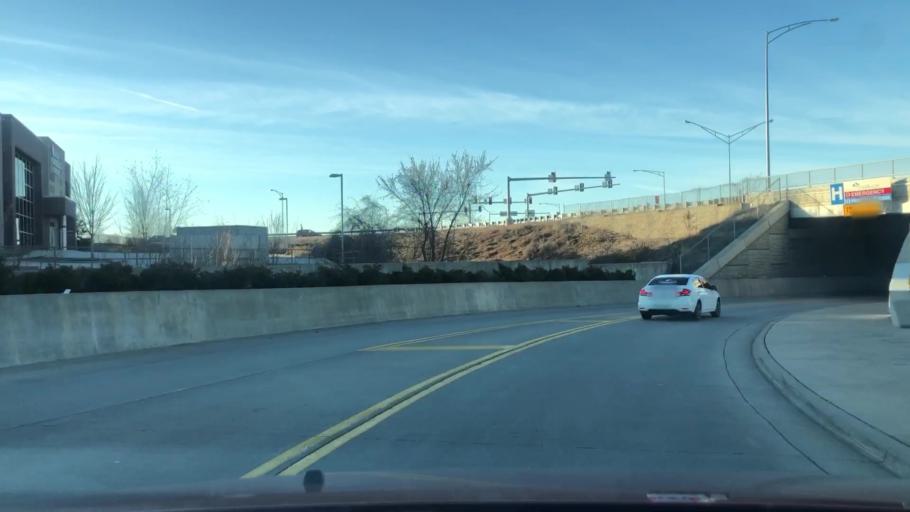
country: US
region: Missouri
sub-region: Greene County
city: Springfield
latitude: 37.1442
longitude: -93.2776
